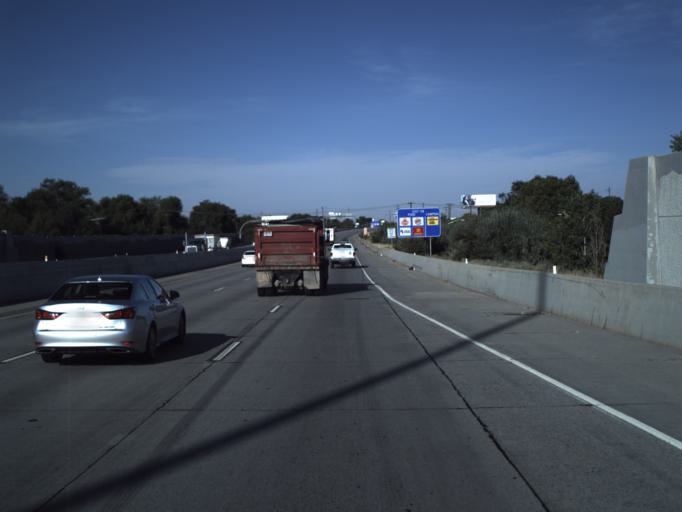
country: US
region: Utah
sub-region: Salt Lake County
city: Salt Lake City
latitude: 40.7647
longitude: -111.9225
